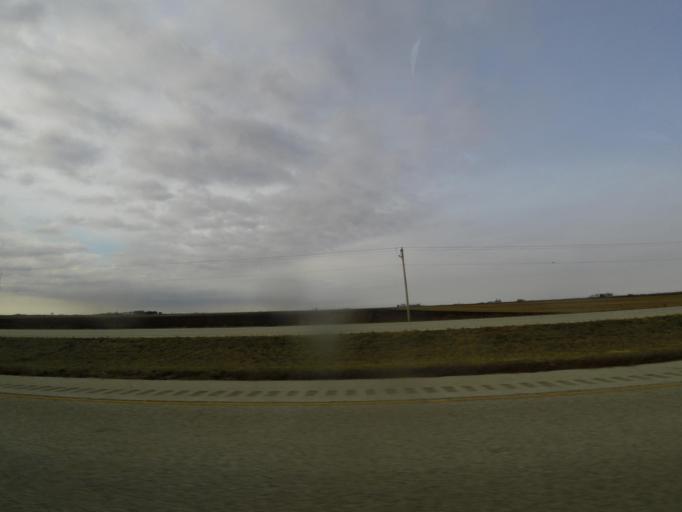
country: US
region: Illinois
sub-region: Christian County
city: Assumption
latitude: 39.4972
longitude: -89.0434
